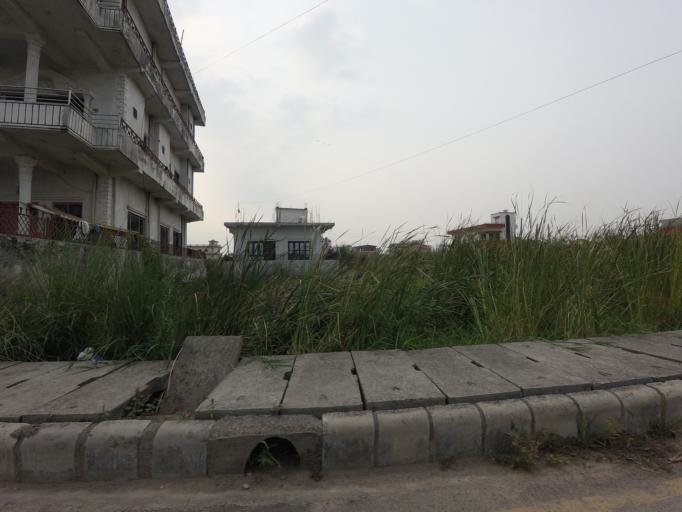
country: NP
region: Western Region
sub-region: Lumbini Zone
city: Bhairahawa
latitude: 27.5205
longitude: 83.4485
